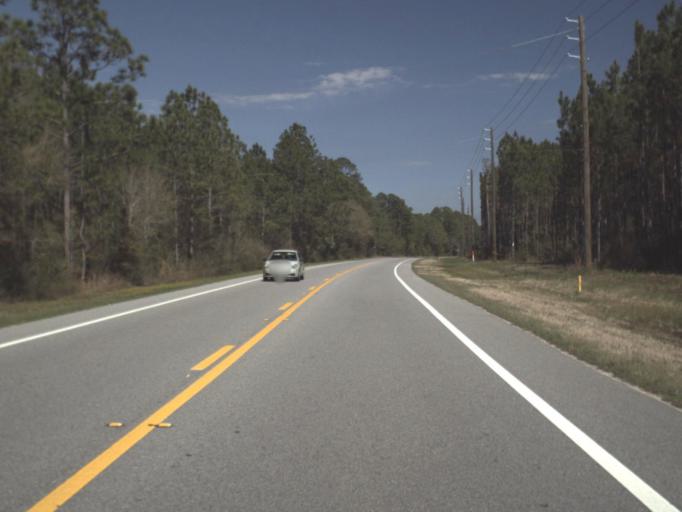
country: US
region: Florida
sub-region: Bay County
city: Lynn Haven
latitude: 30.3282
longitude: -85.7737
